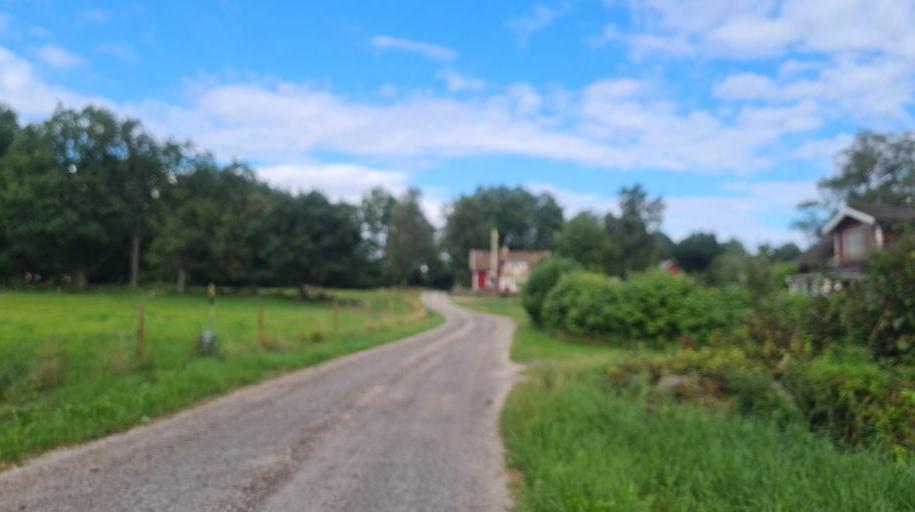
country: SE
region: Kronoberg
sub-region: Ljungby Kommun
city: Ljungby
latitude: 56.8150
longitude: 13.8498
